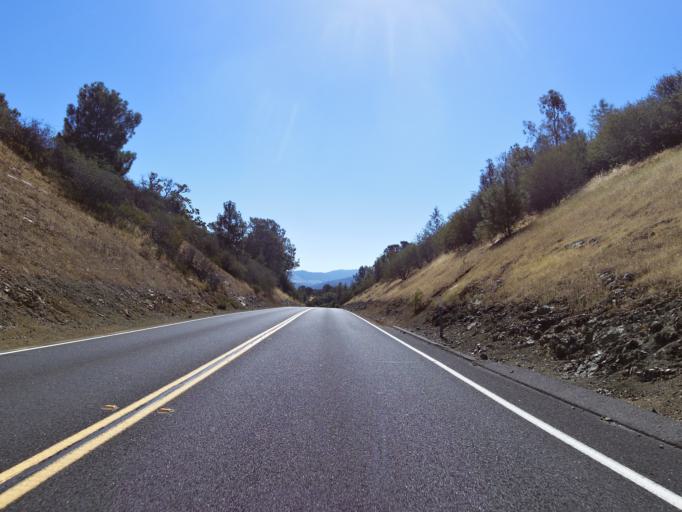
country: US
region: California
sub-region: Tuolumne County
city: Tuolumne City
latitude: 37.6997
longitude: -120.2871
